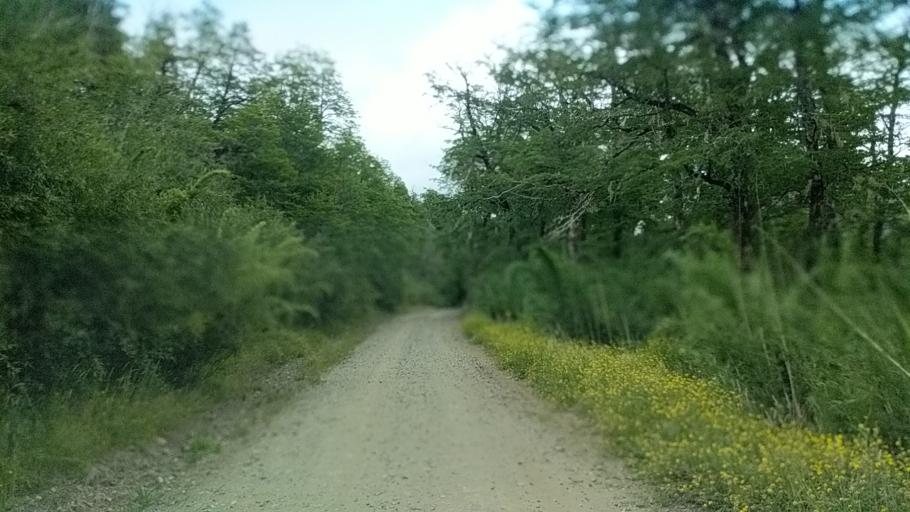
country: AR
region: Neuquen
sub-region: Departamento de Lacar
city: San Martin de los Andes
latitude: -39.8273
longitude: -71.6369
